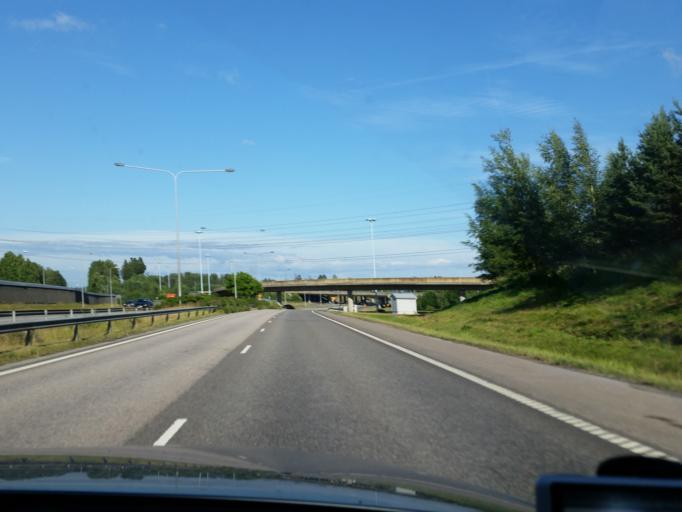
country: FI
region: Uusimaa
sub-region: Helsinki
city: Espoo
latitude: 60.2208
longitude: 24.6389
